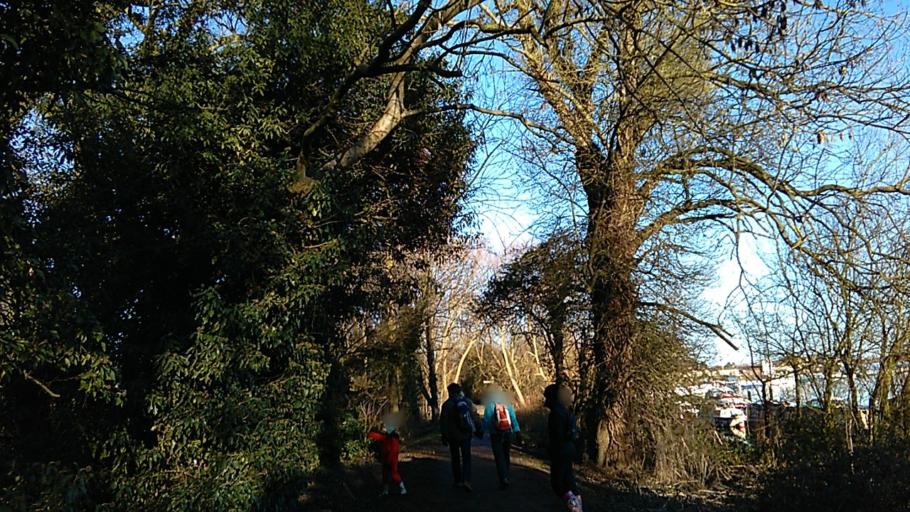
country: GB
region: England
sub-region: Nottinghamshire
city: Gotham
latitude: 52.9116
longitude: -1.2131
